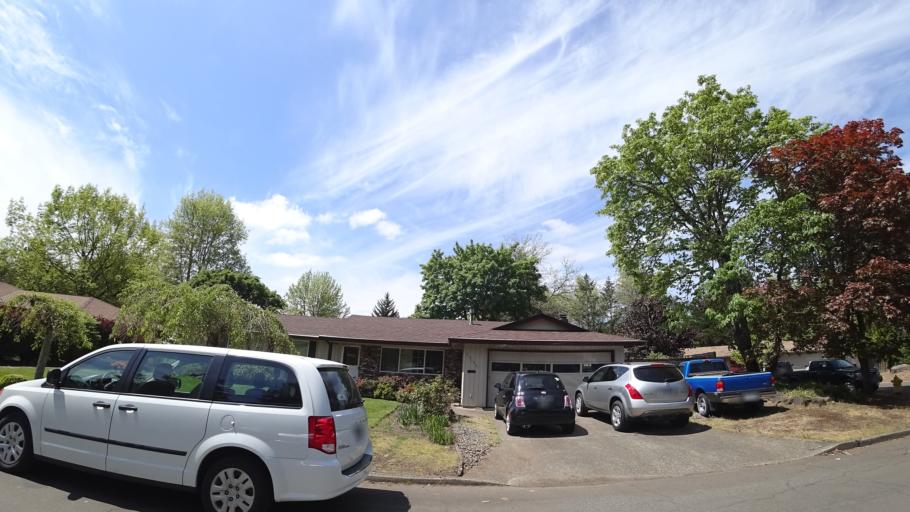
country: US
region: Oregon
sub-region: Washington County
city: Aloha
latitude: 45.4776
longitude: -122.8863
